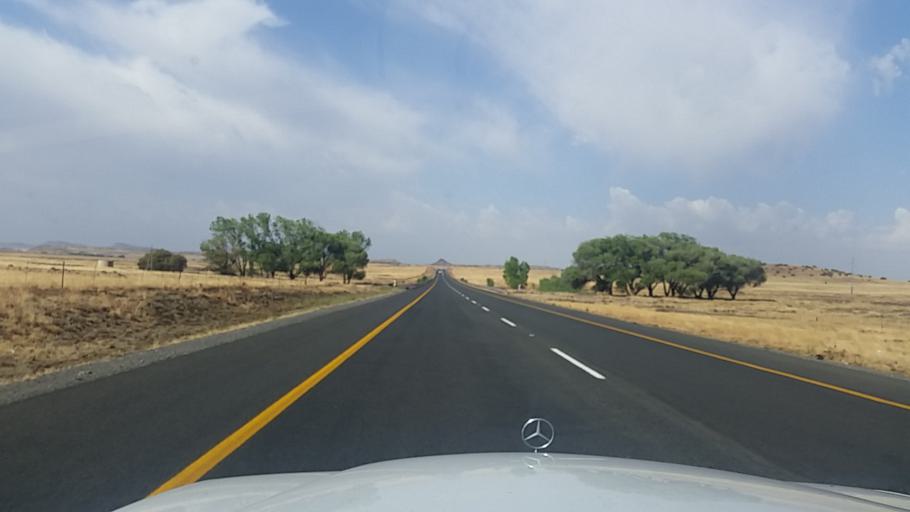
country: ZA
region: Orange Free State
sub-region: Xhariep District Municipality
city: Trompsburg
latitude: -30.3023
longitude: 25.7186
